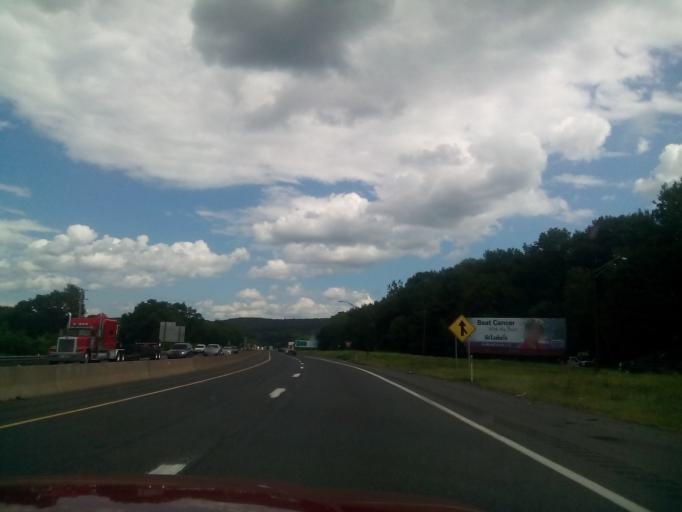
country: US
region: Pennsylvania
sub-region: Monroe County
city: Arlington Heights
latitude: 40.9815
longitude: -75.2123
